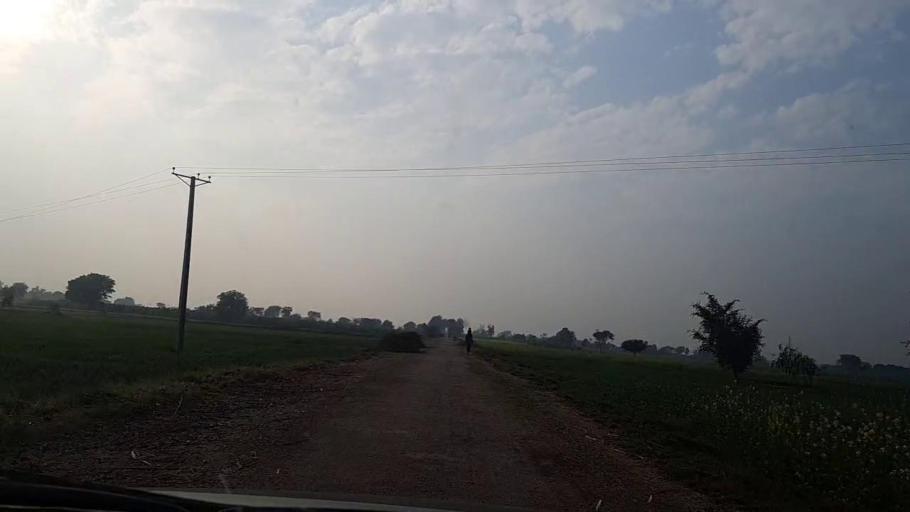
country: PK
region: Sindh
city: Nawabshah
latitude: 26.2740
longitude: 68.3251
